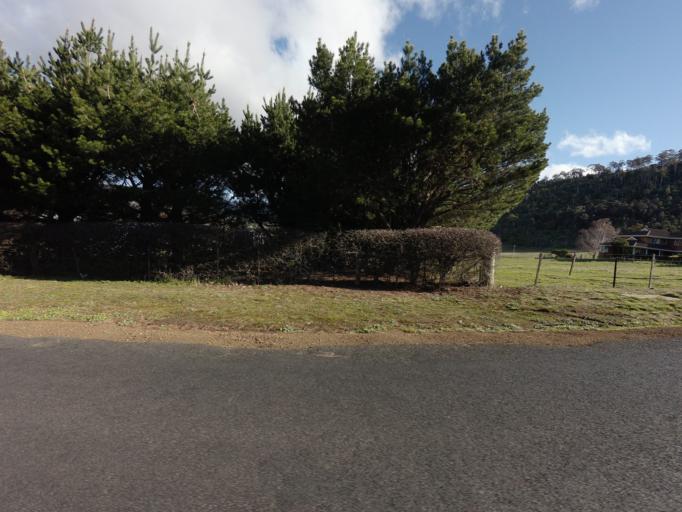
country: AU
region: Tasmania
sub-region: Derwent Valley
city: New Norfolk
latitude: -42.7529
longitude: 147.0478
